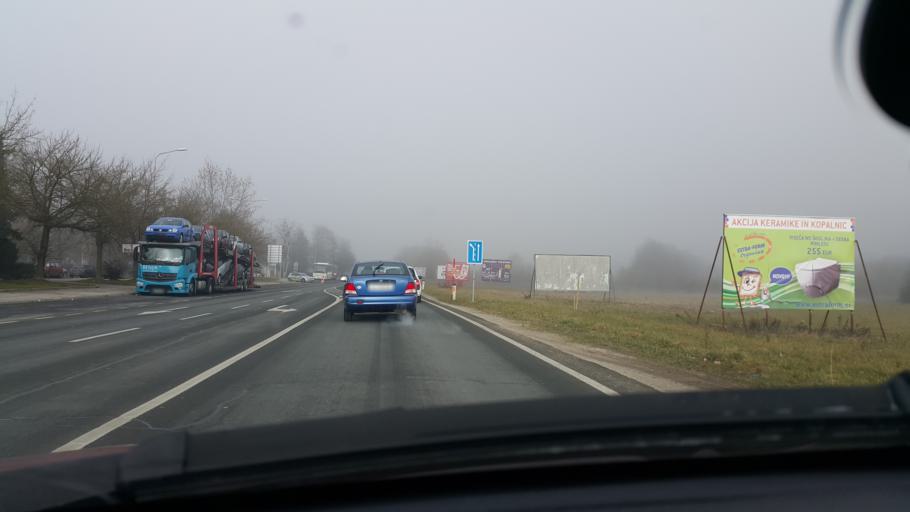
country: SI
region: Brezice
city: Brezice
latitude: 45.9064
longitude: 15.6023
